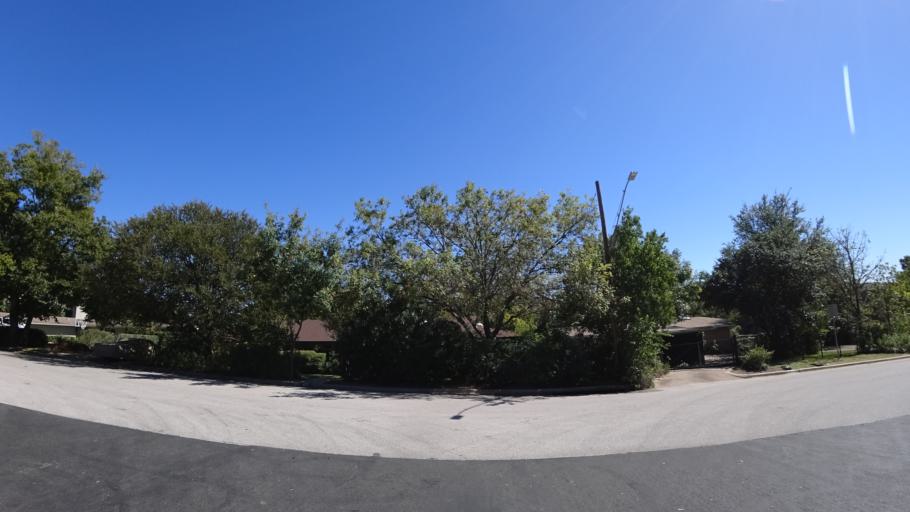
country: US
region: Texas
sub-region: Travis County
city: West Lake Hills
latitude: 30.3266
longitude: -97.7652
